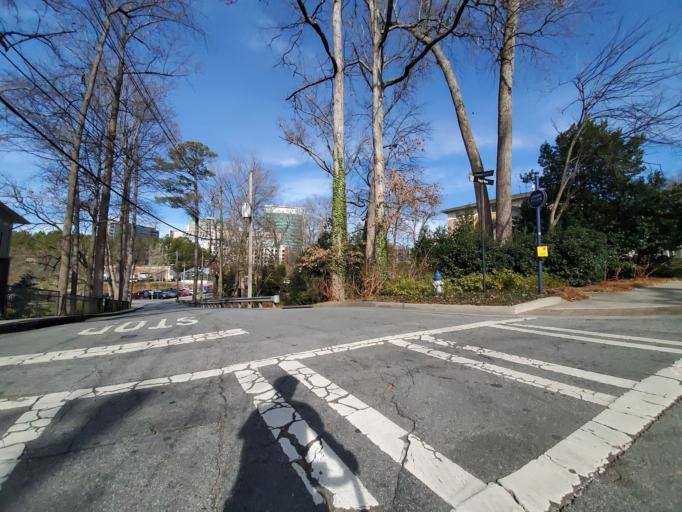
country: US
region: Georgia
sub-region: DeKalb County
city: Druid Hills
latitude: 33.7949
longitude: -84.3277
